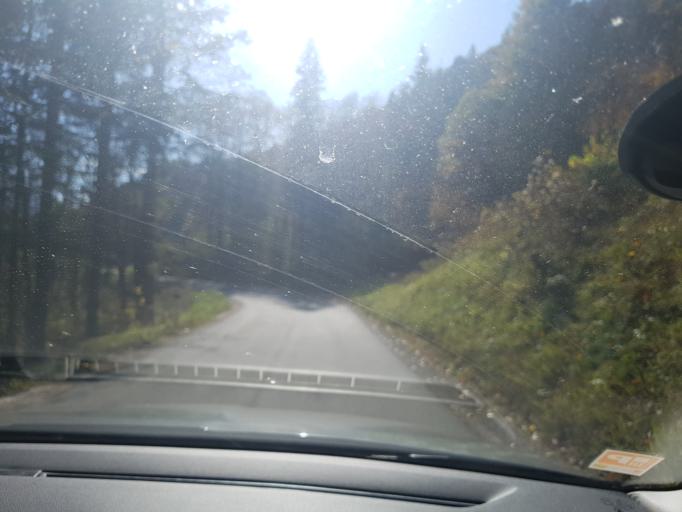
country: AT
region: Tyrol
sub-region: Politischer Bezirk Kitzbuhel
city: Hochfilzen
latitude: 47.4961
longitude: 12.6078
